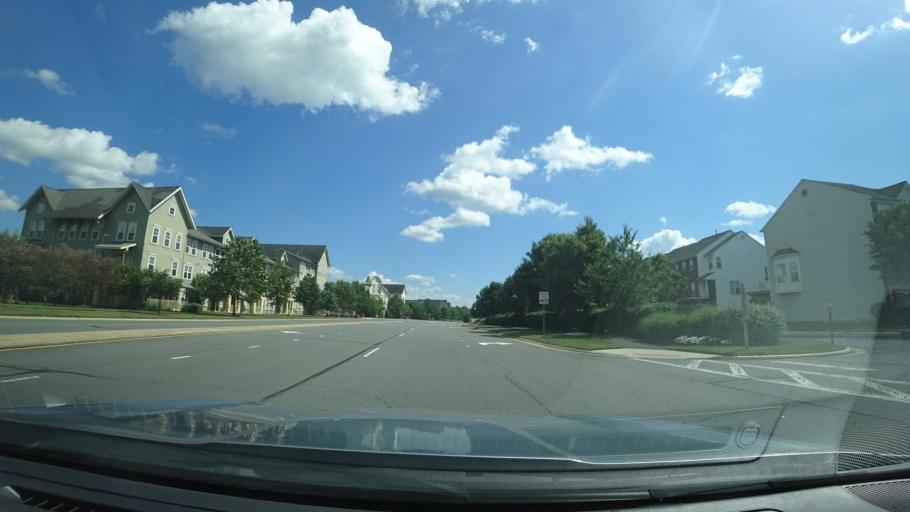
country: US
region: Virginia
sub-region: Loudoun County
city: Broadlands
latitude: 38.9936
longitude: -77.4858
